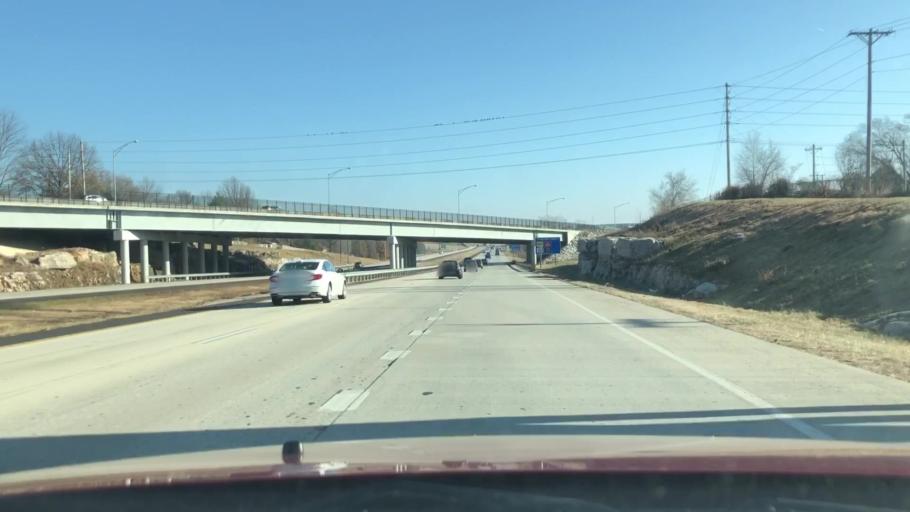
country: US
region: Missouri
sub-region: Greene County
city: Springfield
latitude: 37.1381
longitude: -93.2899
